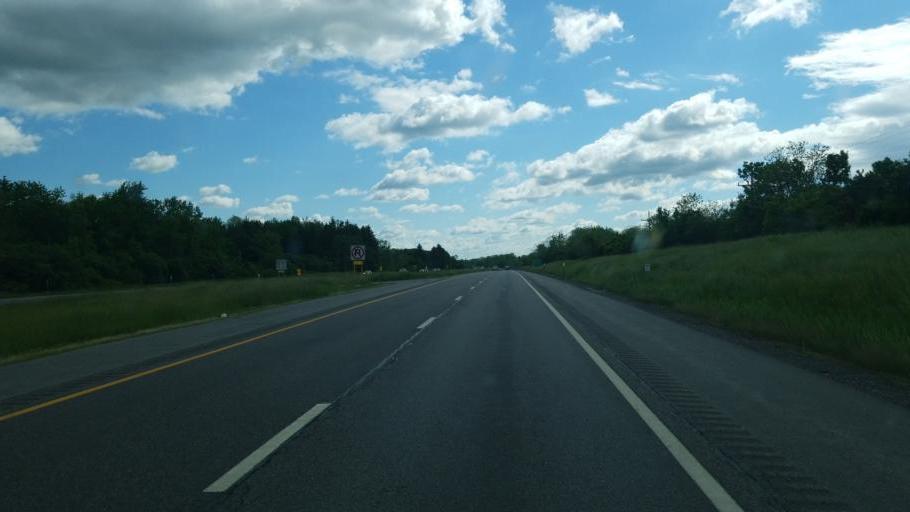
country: US
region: New York
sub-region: Cayuga County
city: Port Byron
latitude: 43.0297
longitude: -76.6568
